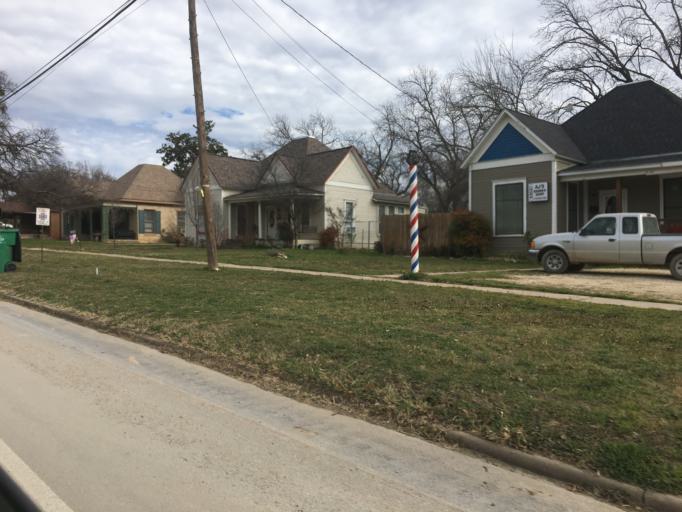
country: US
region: Texas
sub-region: Erath County
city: Dublin
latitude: 32.0874
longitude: -98.3416
